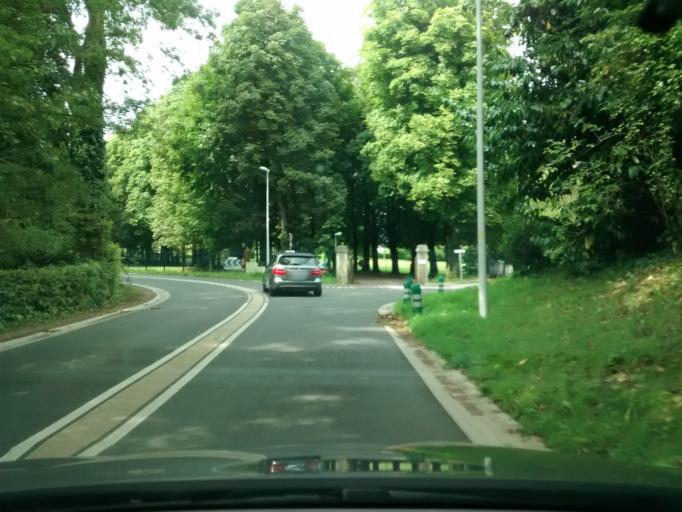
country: FR
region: Lower Normandy
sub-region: Departement du Calvados
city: Blonville-sur-Mer
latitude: 49.3358
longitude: 0.0529
